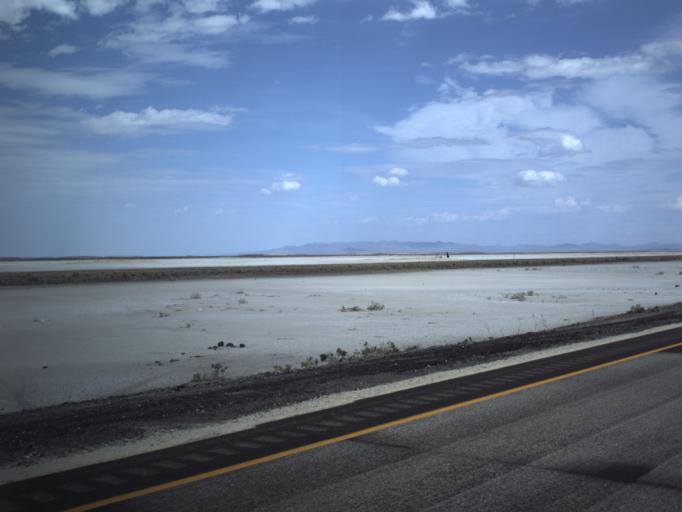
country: US
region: Utah
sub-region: Tooele County
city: Wendover
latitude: 40.7305
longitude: -113.4850
